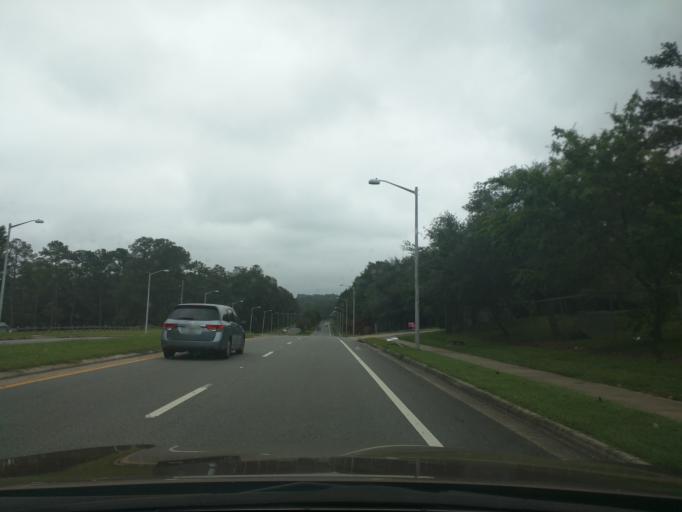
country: US
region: Florida
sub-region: Leon County
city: Tallahassee
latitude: 30.4400
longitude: -84.2161
